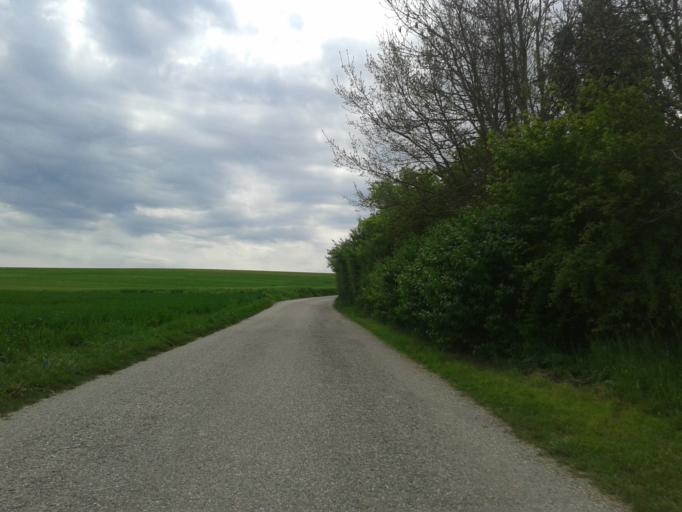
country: DE
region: Baden-Wuerttemberg
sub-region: Tuebingen Region
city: Erbach
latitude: 48.3476
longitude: 9.9004
